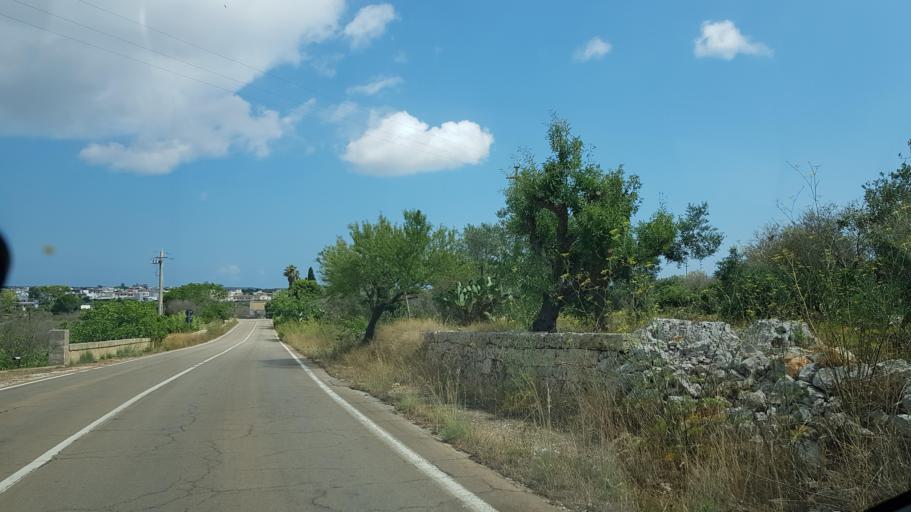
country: IT
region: Apulia
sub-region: Provincia di Lecce
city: Patu
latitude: 39.8447
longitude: 18.3281
